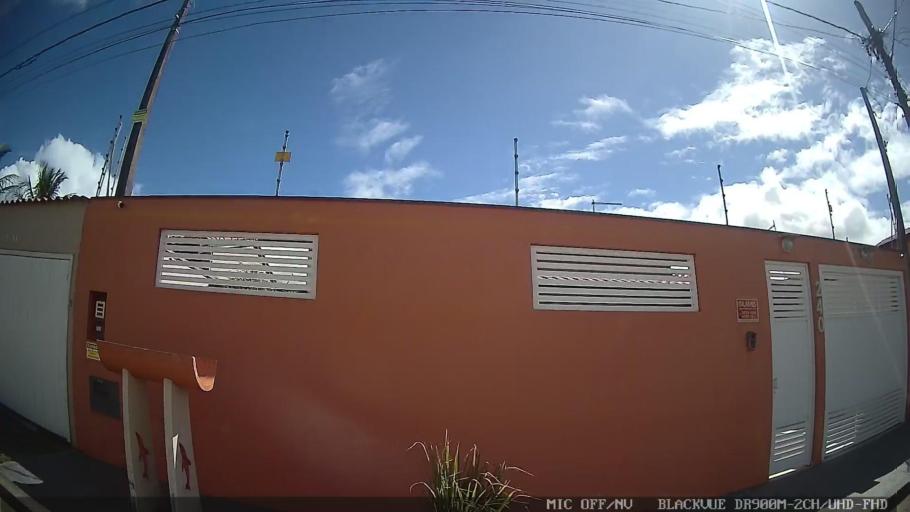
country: BR
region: Sao Paulo
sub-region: Itanhaem
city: Itanhaem
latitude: -24.2248
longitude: -46.8600
